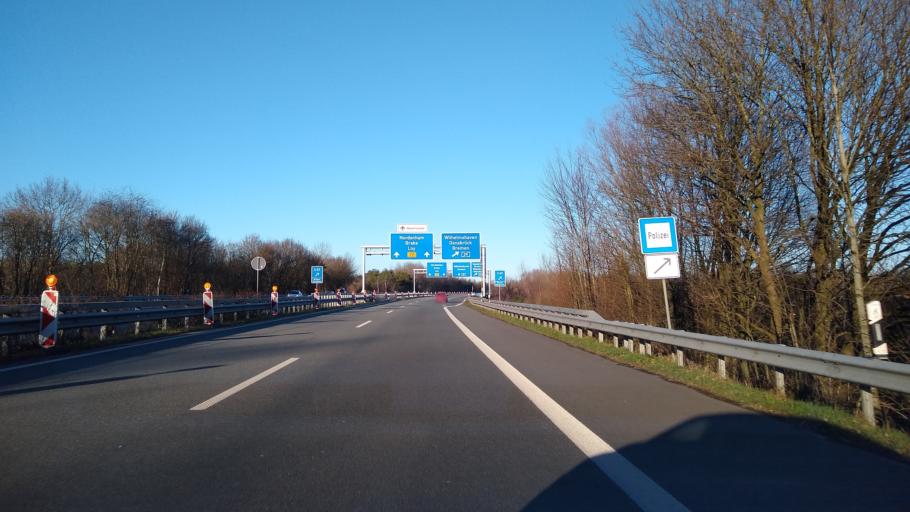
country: DE
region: Lower Saxony
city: Rastede
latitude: 53.2041
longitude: 8.2210
